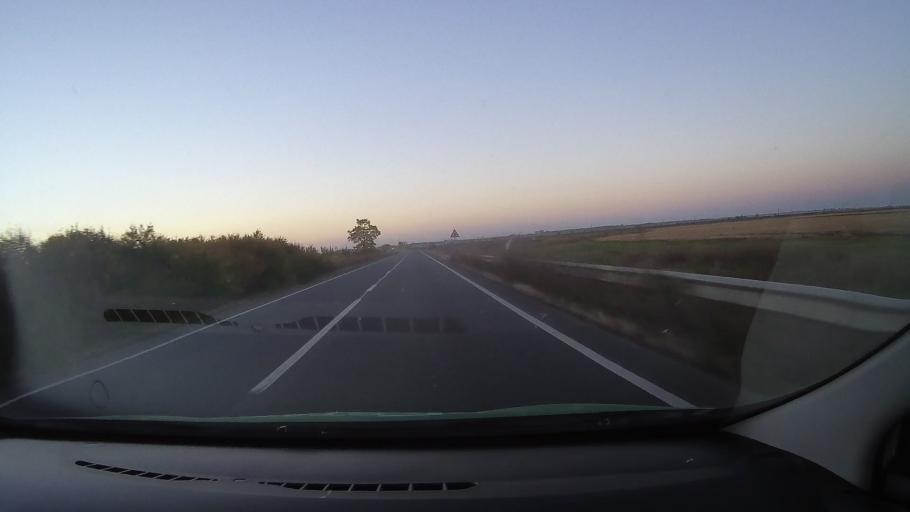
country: RO
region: Bihor
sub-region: Comuna Tarcea
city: Tarcea
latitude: 47.4416
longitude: 22.1916
